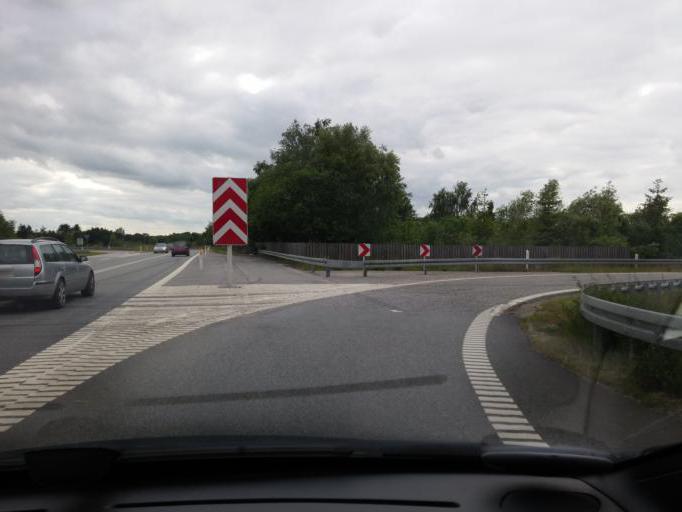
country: DK
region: Capital Region
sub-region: Hillerod Kommune
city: Hillerod
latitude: 55.9550
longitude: 12.2454
